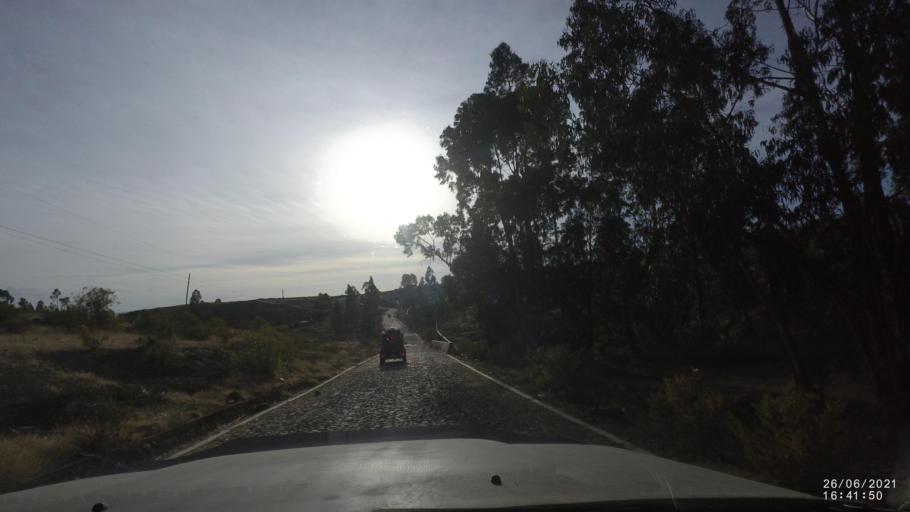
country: BO
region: Cochabamba
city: Arani
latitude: -17.7656
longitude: -65.8230
